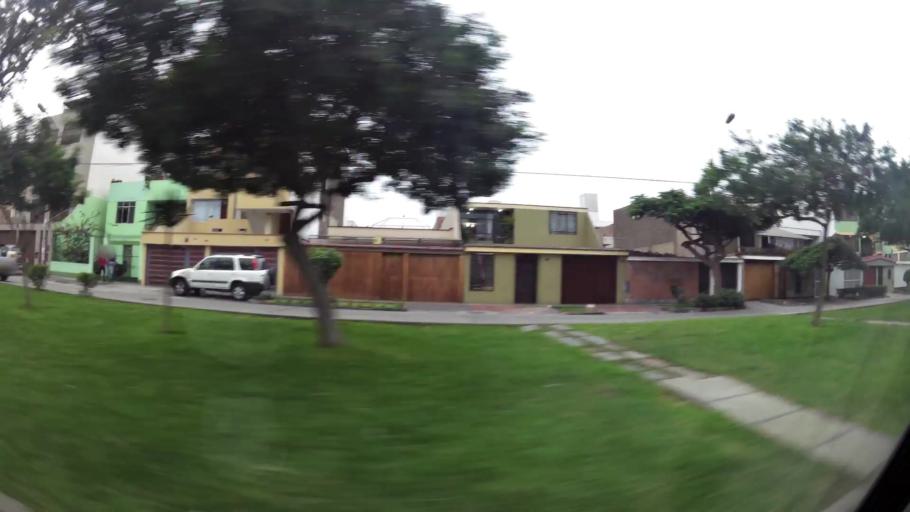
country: PE
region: Lima
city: Lima
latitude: -12.0650
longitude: -77.0672
